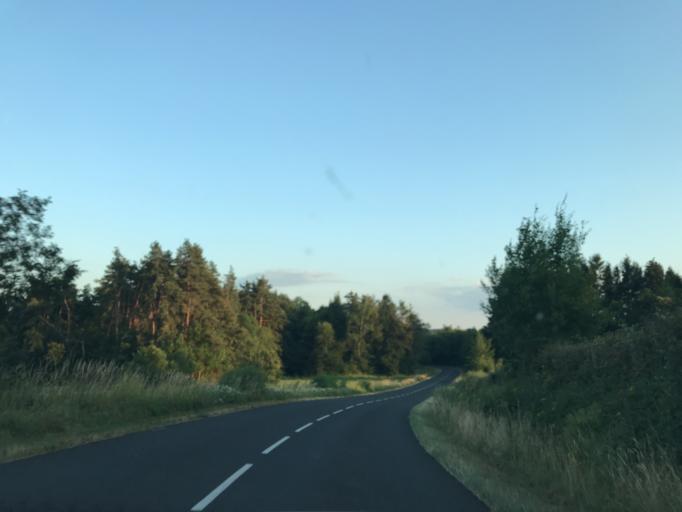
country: FR
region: Auvergne
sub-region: Departement du Puy-de-Dome
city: Courpiere
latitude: 45.7523
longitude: 3.6042
